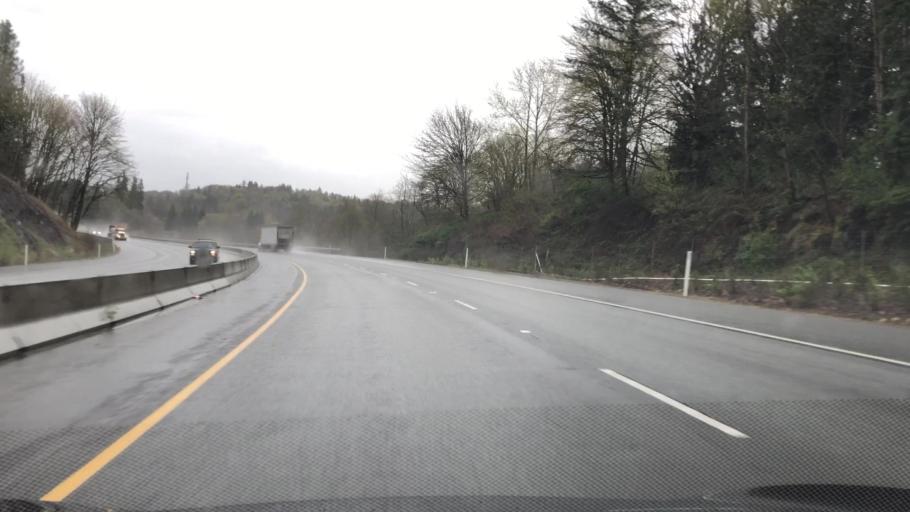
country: US
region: Washington
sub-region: Snohomish County
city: Cathcart
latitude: 47.8344
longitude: -122.0342
